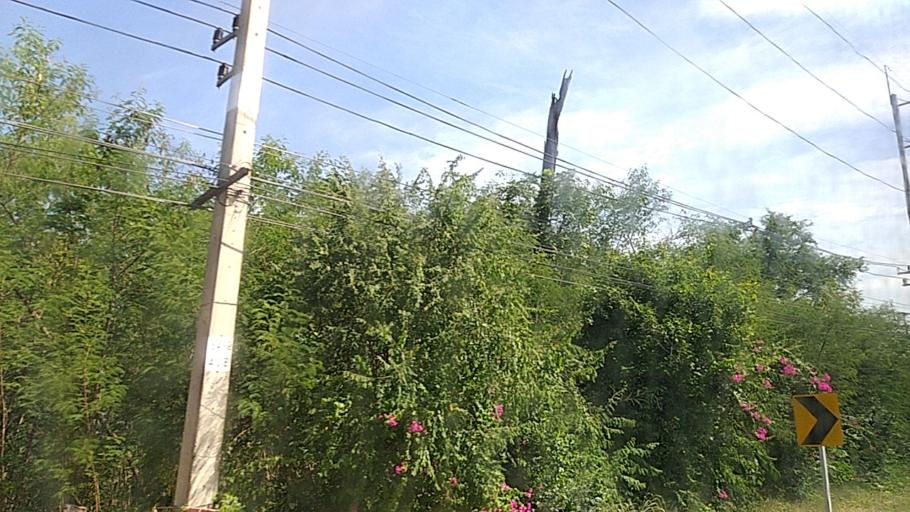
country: TH
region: Khon Kaen
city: Khon Kaen
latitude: 16.4469
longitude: 102.9573
